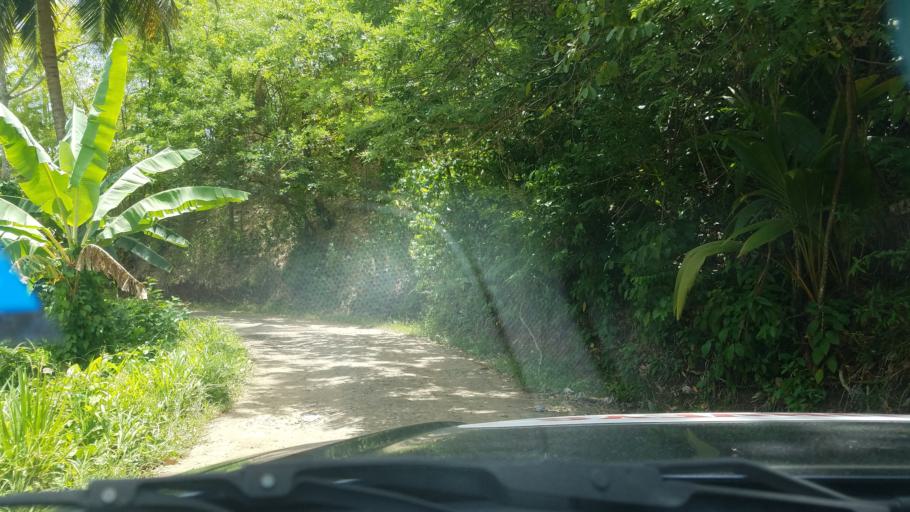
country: LC
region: Castries Quarter
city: Bisee
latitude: 14.0005
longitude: -60.9190
